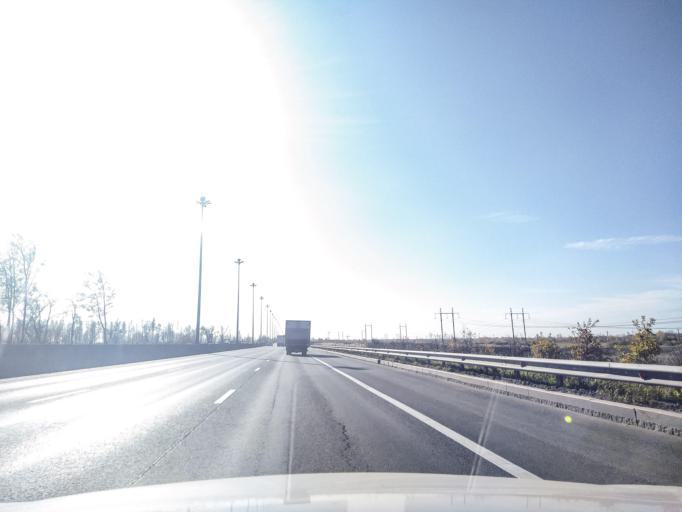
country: RU
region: St.-Petersburg
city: Aleksandrovskaya
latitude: 59.7114
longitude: 30.2749
